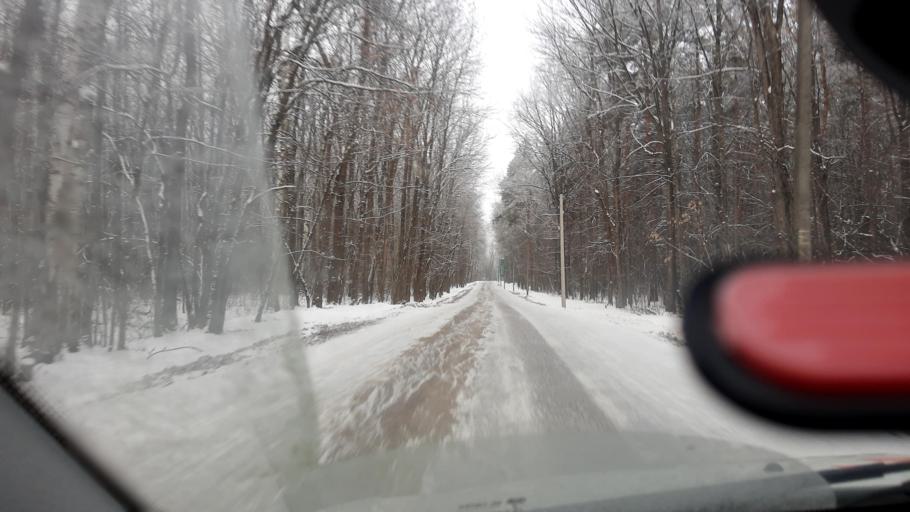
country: RU
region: Bashkortostan
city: Ufa
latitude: 54.7041
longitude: 55.9239
